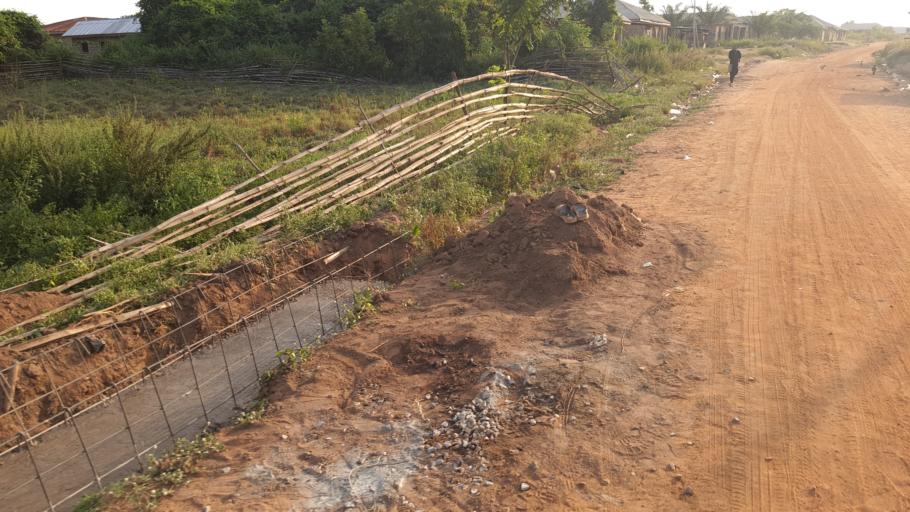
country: NG
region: Osun
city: Iwo
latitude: 7.6204
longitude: 4.1591
